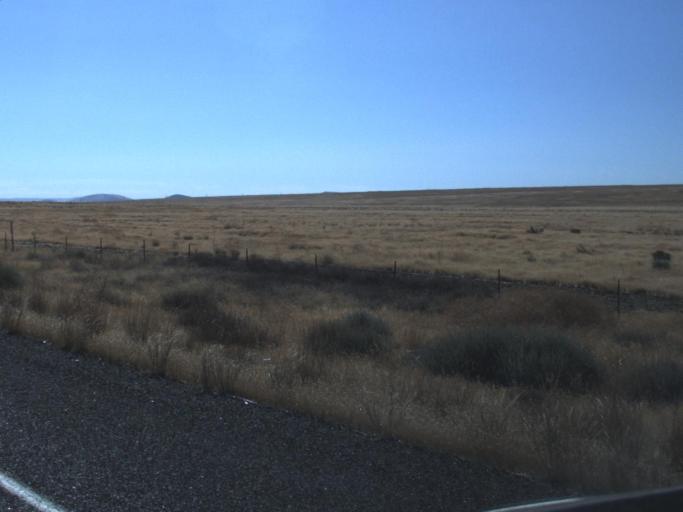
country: US
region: Washington
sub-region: Benton County
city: Benton City
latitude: 46.4468
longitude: -119.4985
